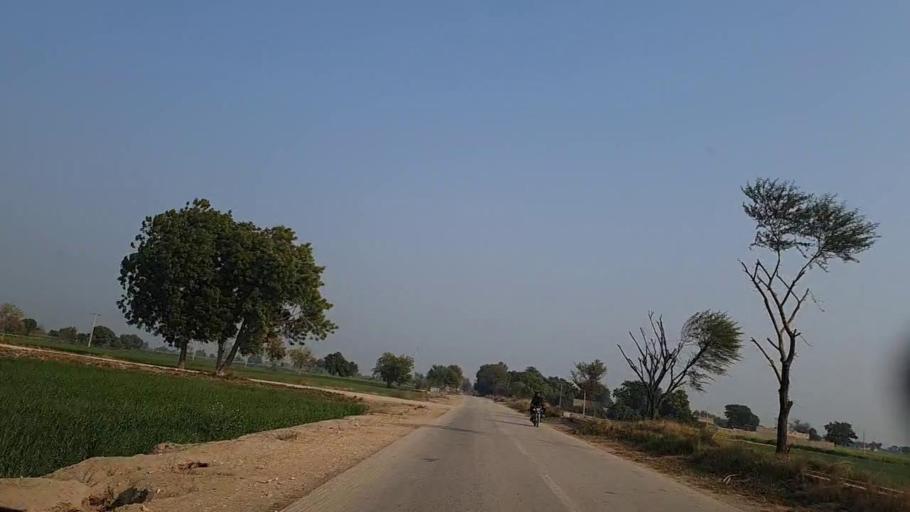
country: PK
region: Sindh
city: Sakrand
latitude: 26.1334
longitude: 68.2040
